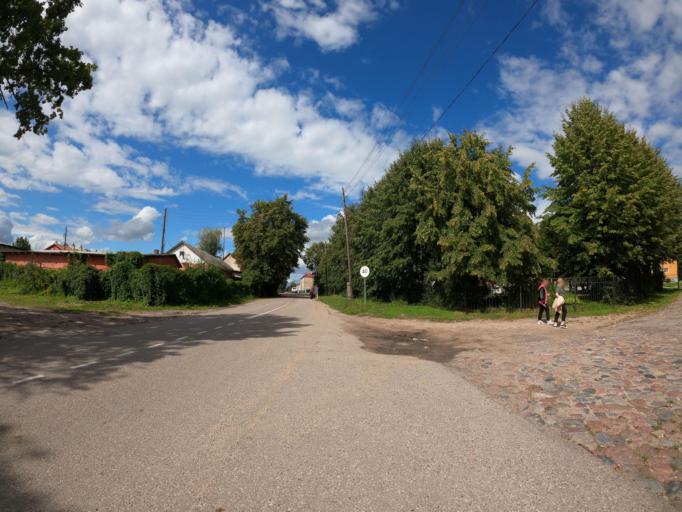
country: RU
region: Kaliningrad
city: Zheleznodorozhnyy
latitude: 54.3624
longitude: 21.3021
